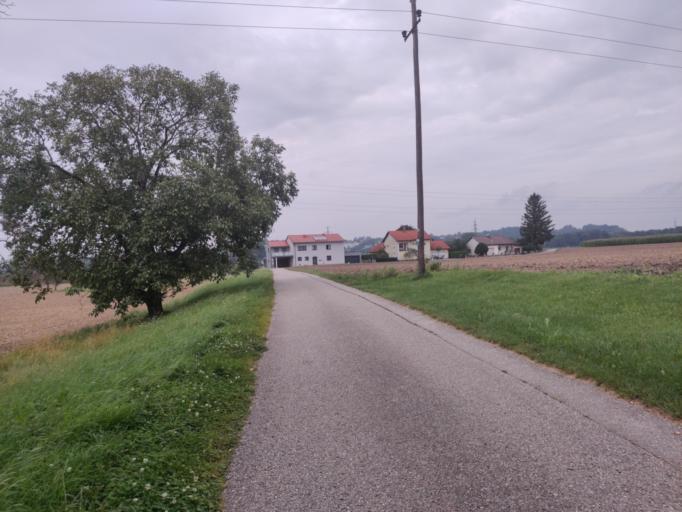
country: AT
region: Lower Austria
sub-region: Politischer Bezirk Amstetten
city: Ennsdorf
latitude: 48.2276
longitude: 14.5167
